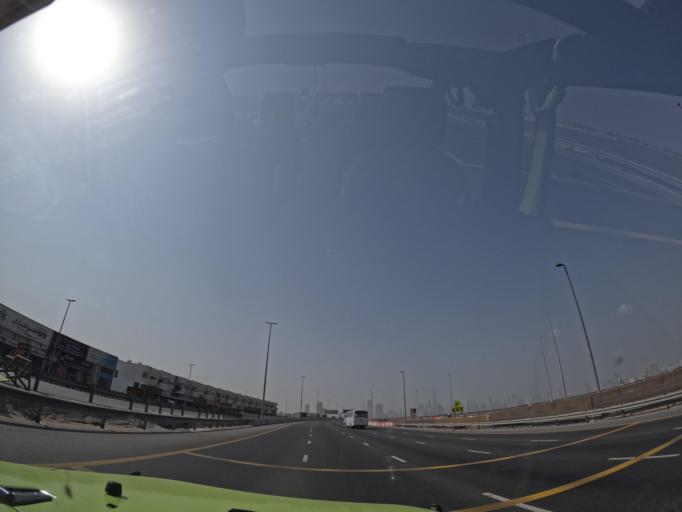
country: AE
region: Ash Shariqah
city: Sharjah
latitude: 25.1856
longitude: 55.3428
